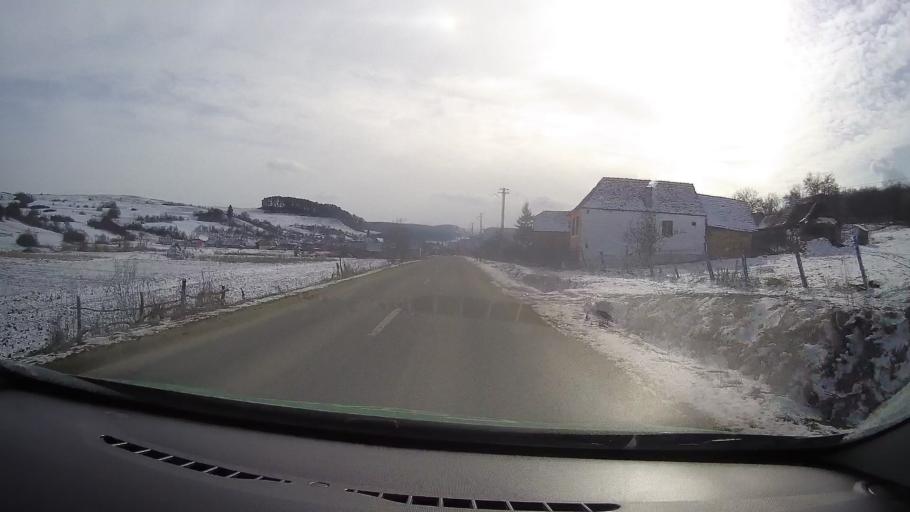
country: RO
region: Sibiu
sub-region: Comuna Bradeni
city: Bradeni
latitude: 46.0889
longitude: 24.8333
